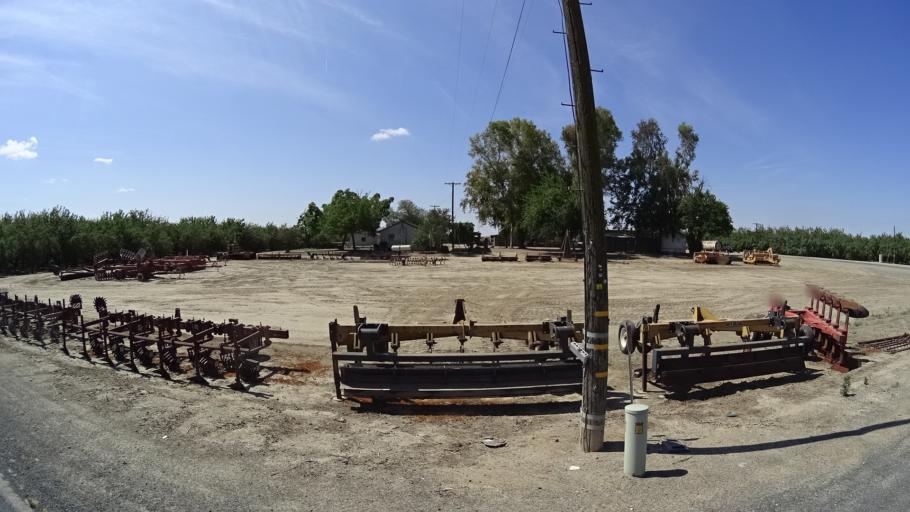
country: US
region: California
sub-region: Kings County
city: Armona
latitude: 36.2693
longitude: -119.7297
